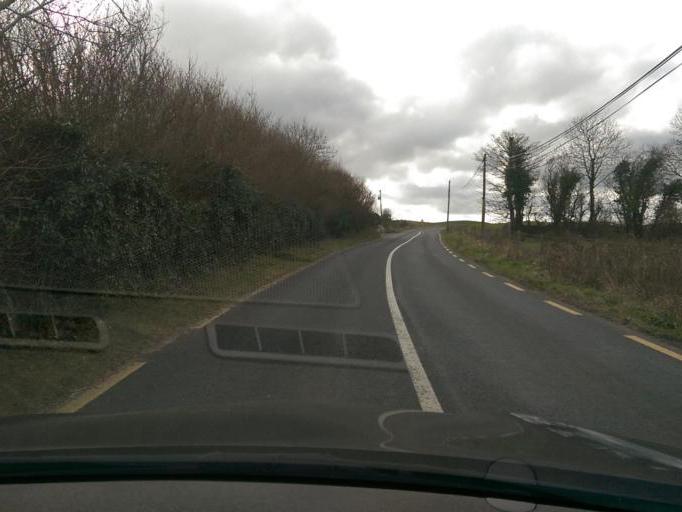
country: IE
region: Connaught
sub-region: County Galway
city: Ballinasloe
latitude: 53.3269
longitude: -8.4119
